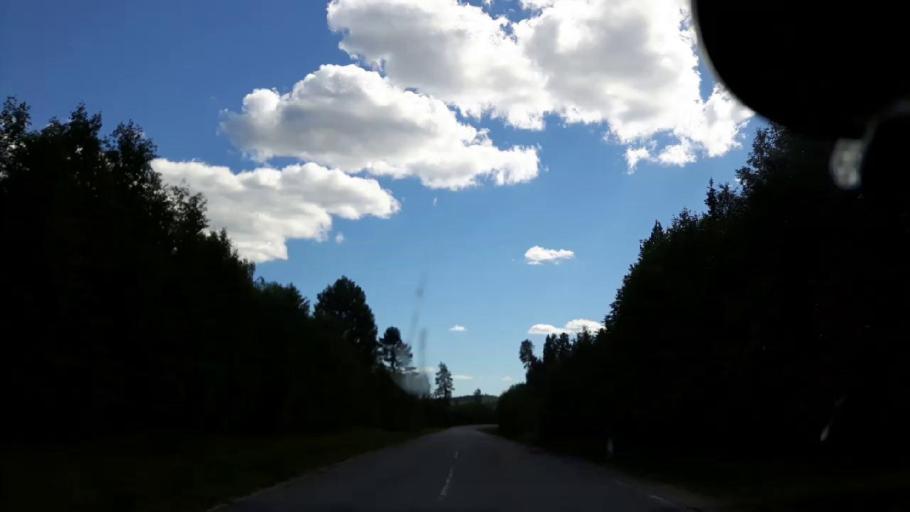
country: SE
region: Jaemtland
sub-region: Ragunda Kommun
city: Hammarstrand
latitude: 62.8426
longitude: 16.1729
